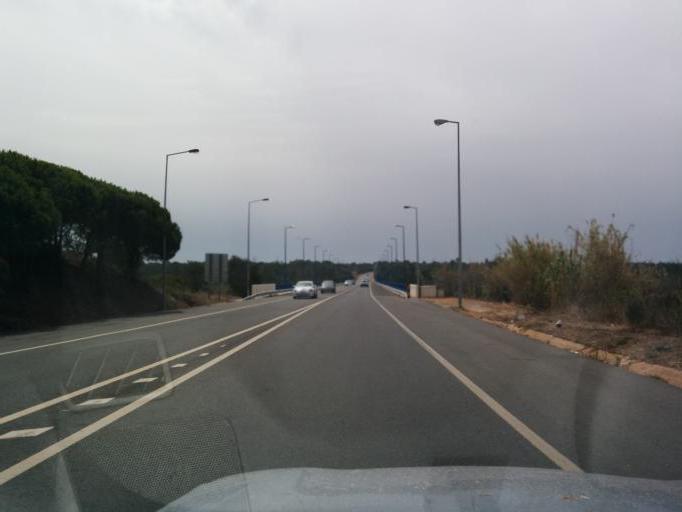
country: PT
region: Beja
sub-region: Odemira
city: Vila Nova de Milfontes
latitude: 37.7289
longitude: -8.7711
